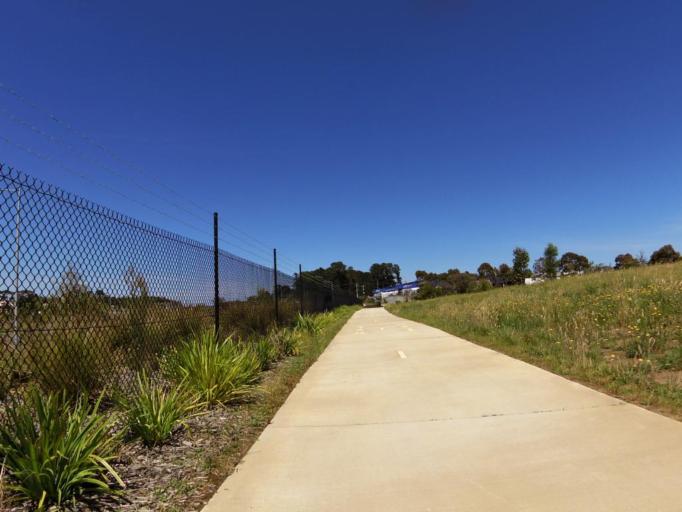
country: AU
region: Victoria
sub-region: Frankston
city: Langwarrin
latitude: -38.1528
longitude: 145.1692
